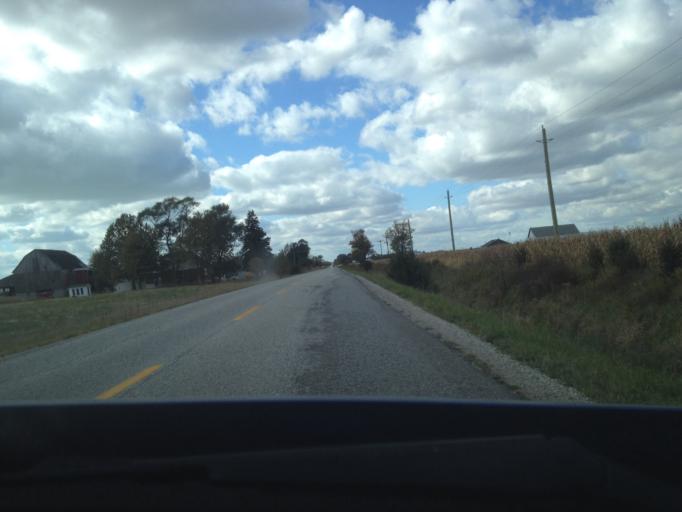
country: US
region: Michigan
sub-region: Wayne County
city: Grosse Pointe
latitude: 42.0314
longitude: -82.5340
